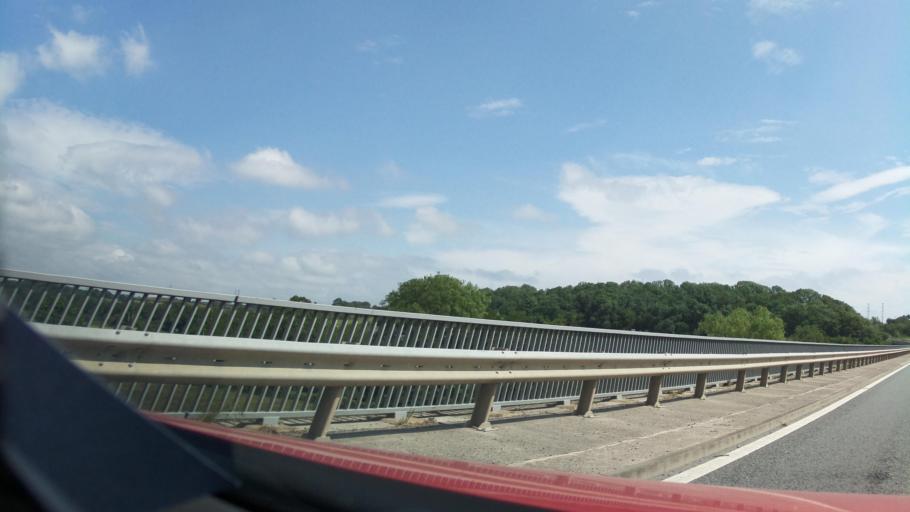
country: GB
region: Wales
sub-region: Vale of Glamorgan
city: Cowbridge
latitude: 51.4638
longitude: -3.4433
